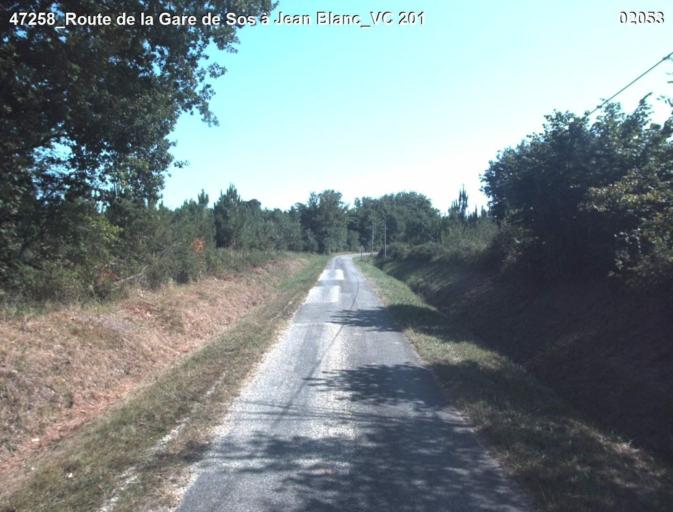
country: FR
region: Midi-Pyrenees
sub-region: Departement du Gers
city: Montreal
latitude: 44.0302
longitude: 0.1589
